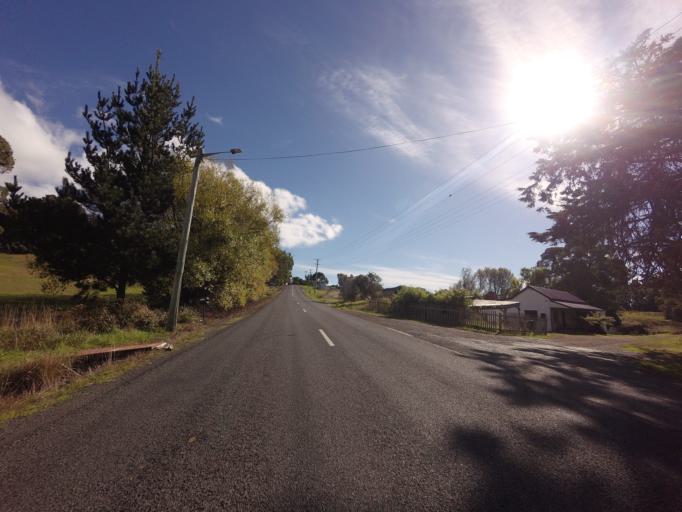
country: AU
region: Tasmania
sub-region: Clarence
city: Sandford
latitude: -43.0593
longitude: 147.8106
